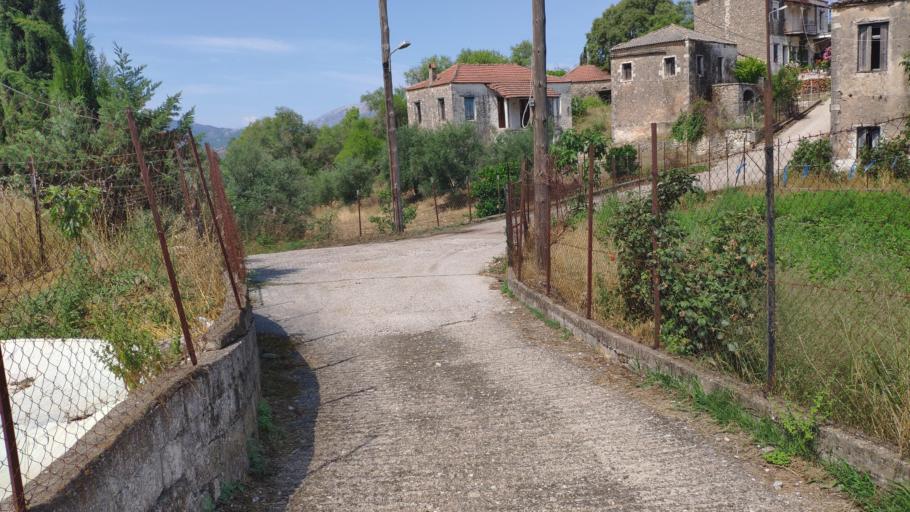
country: GR
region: West Greece
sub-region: Nomos Aitolias kai Akarnanias
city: Fitiai
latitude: 38.7074
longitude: 21.1730
